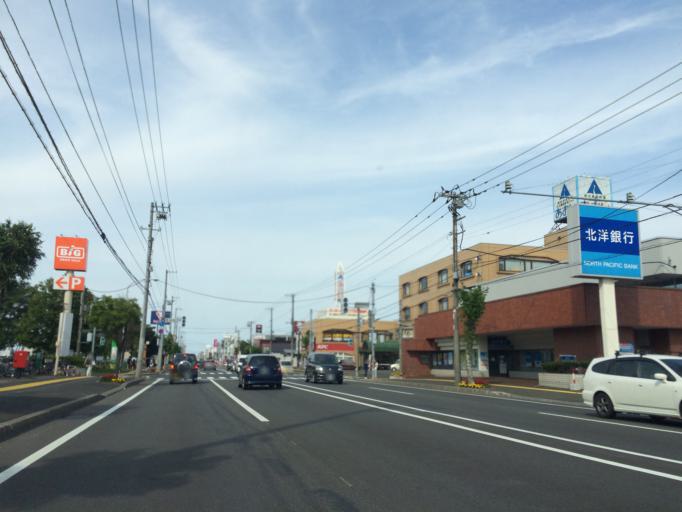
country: JP
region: Hokkaido
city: Ebetsu
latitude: 43.0947
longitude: 141.5259
